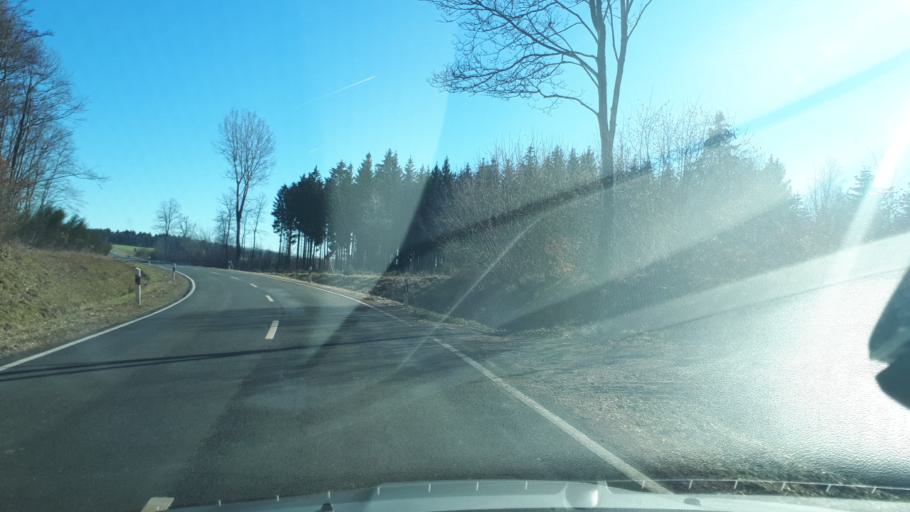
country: DE
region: Rheinland-Pfalz
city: Brockscheid
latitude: 50.1308
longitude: 6.8634
